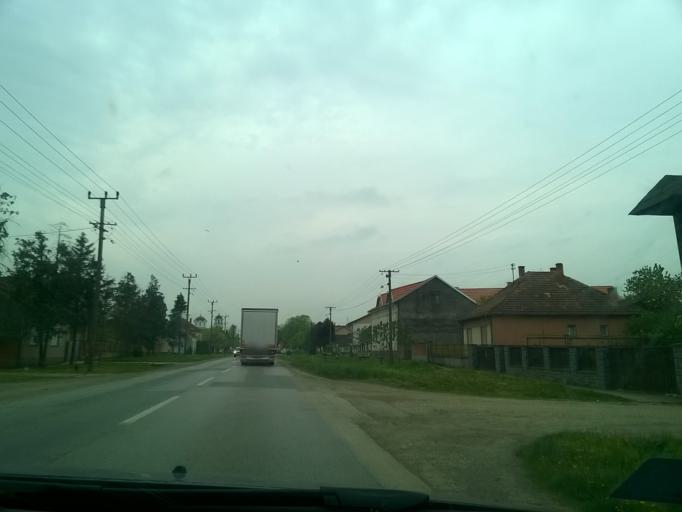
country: RS
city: Hrtkovci
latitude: 44.8841
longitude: 19.7634
